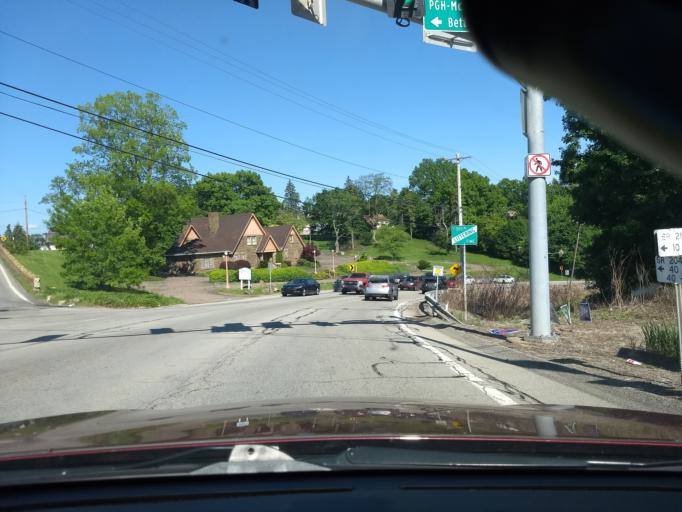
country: US
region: Pennsylvania
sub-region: Allegheny County
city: Dravosburg
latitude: 40.3560
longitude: -79.8984
